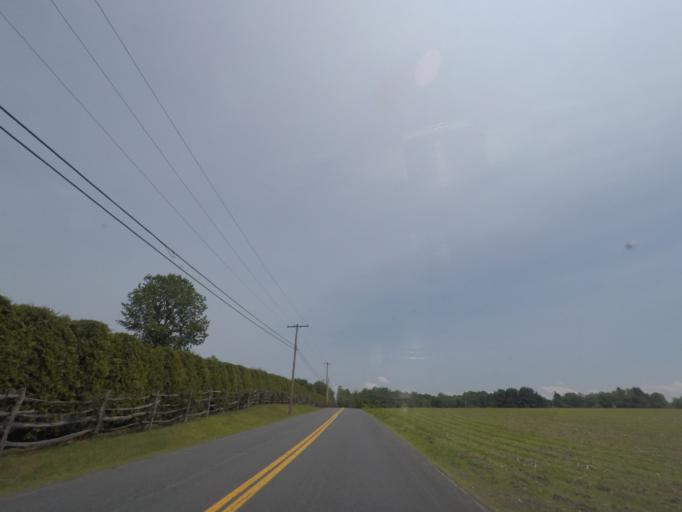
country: US
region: New York
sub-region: Columbia County
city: Niverville
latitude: 42.4748
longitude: -73.6929
